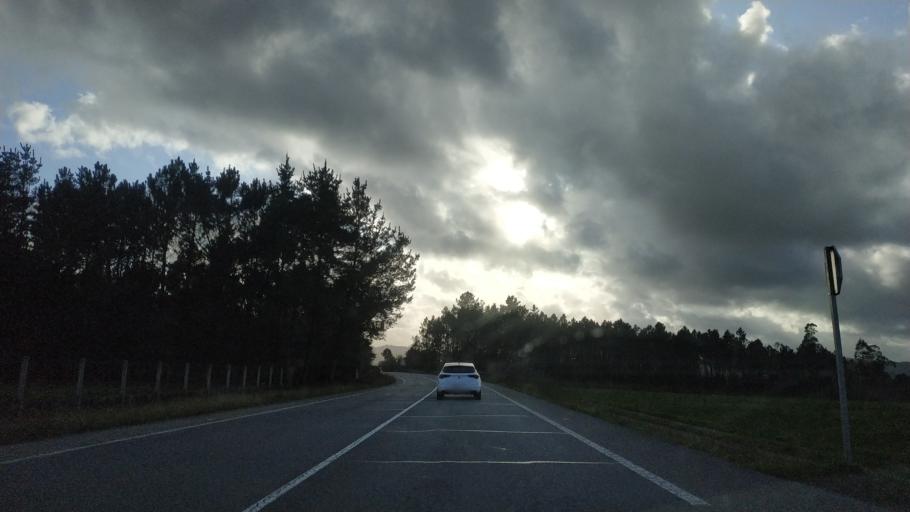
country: ES
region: Galicia
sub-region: Provincia da Coruna
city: Arzua
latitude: 42.9161
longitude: -8.1684
